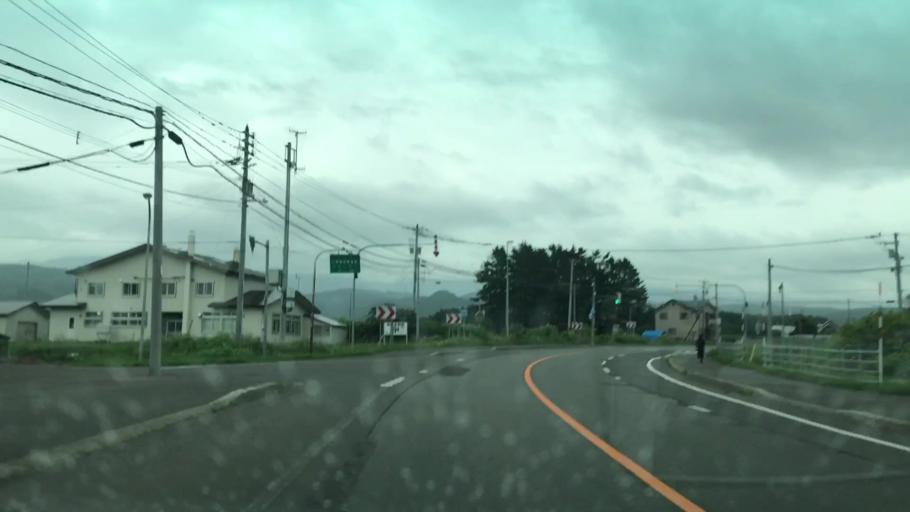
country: JP
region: Hokkaido
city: Niseko Town
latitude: 42.8129
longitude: 140.5440
